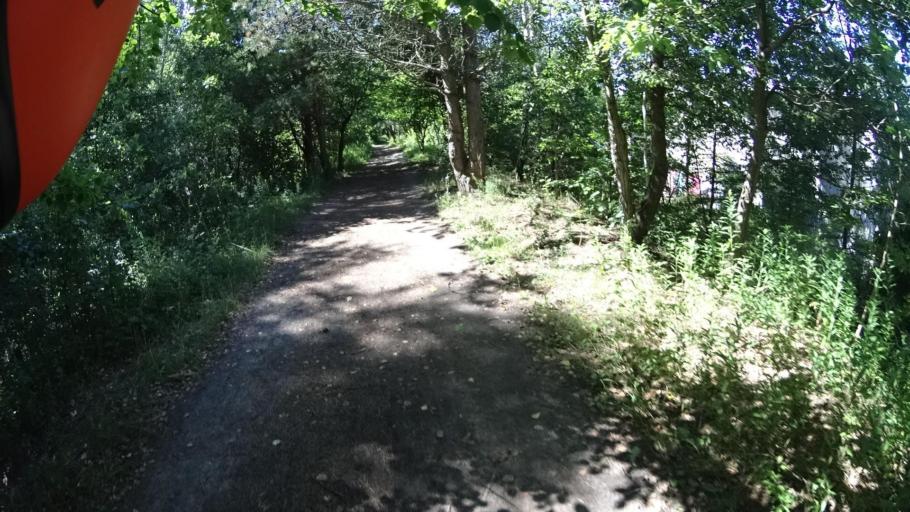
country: PL
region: Masovian Voivodeship
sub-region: Warszawa
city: Kabaty
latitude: 52.1249
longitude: 21.0657
